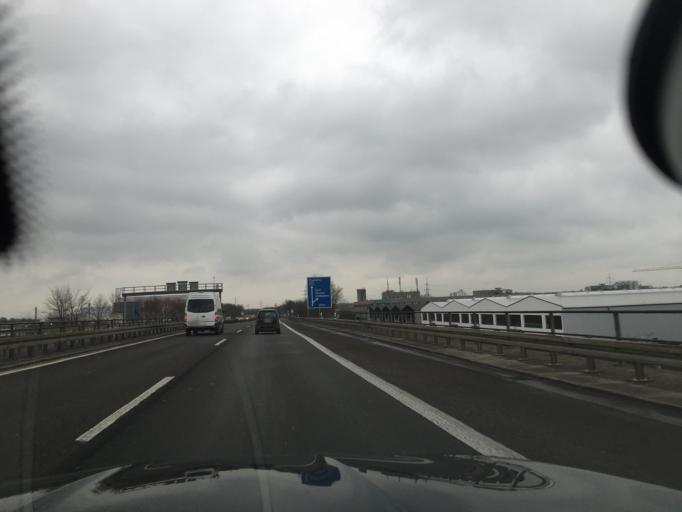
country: DE
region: North Rhine-Westphalia
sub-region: Regierungsbezirk Koln
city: Gremberghoven
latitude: 50.9171
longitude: 7.0644
